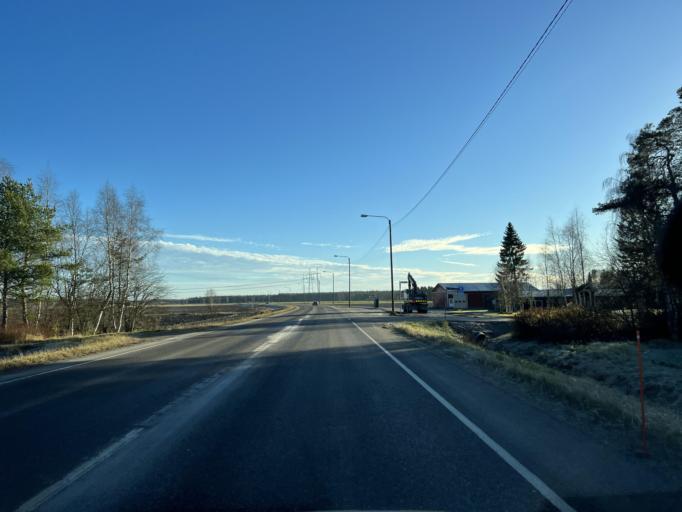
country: FI
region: Northern Ostrobothnia
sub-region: Nivala-Haapajaervi
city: Nivala
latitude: 63.9558
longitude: 24.8616
